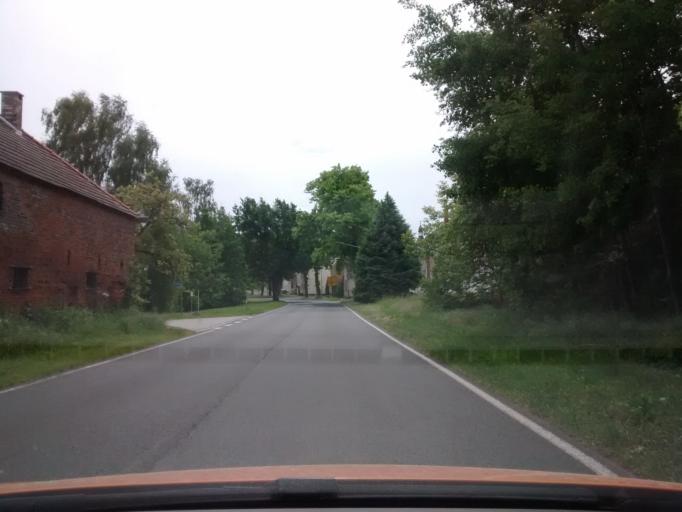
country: DE
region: Brandenburg
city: Juterbog
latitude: 51.9062
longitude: 13.1391
